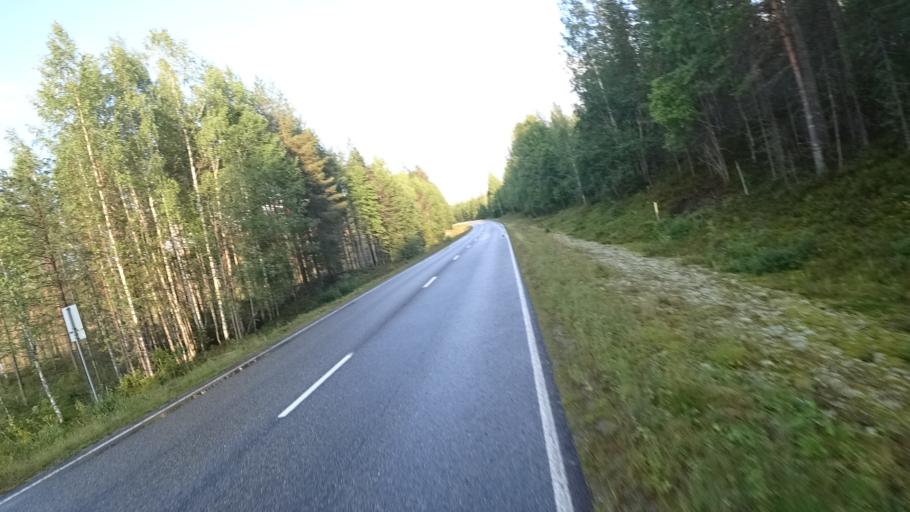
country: FI
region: North Karelia
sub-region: Joensuu
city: Ilomantsi
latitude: 62.6246
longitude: 31.1138
